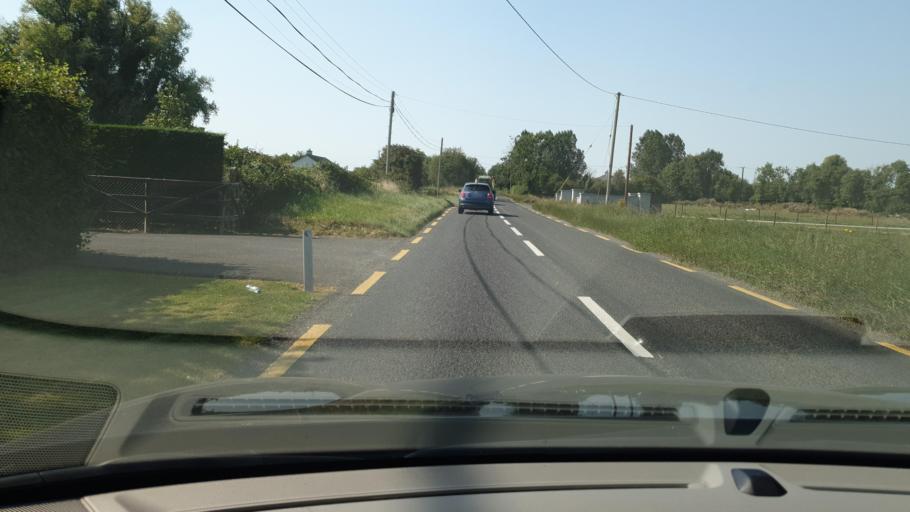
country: IE
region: Leinster
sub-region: An Mhi
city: Trim
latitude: 53.5763
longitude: -6.8334
